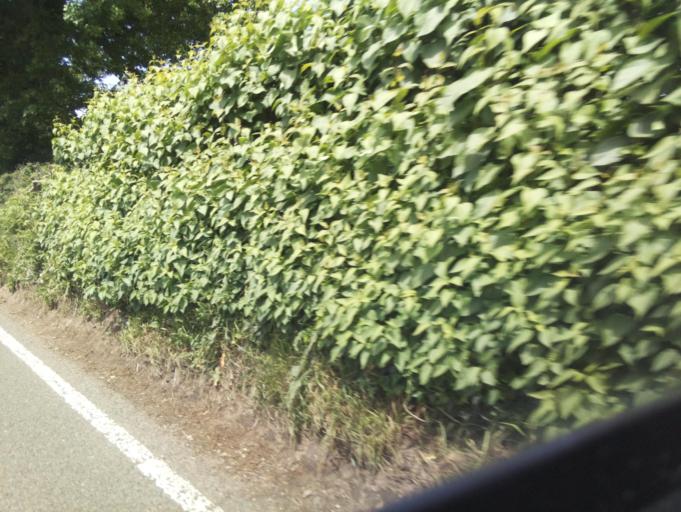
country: GB
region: England
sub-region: Devon
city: Uffculme
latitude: 50.8405
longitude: -3.3117
